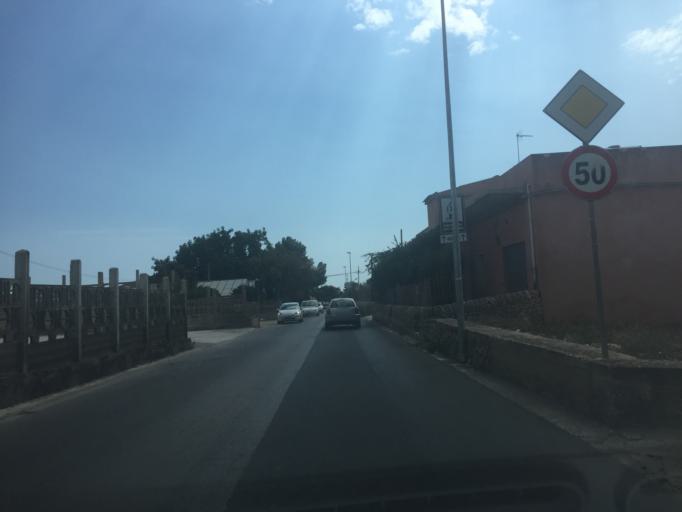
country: IT
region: Sicily
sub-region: Ragusa
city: Santa Croce Camerina
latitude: 36.8210
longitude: 14.5193
